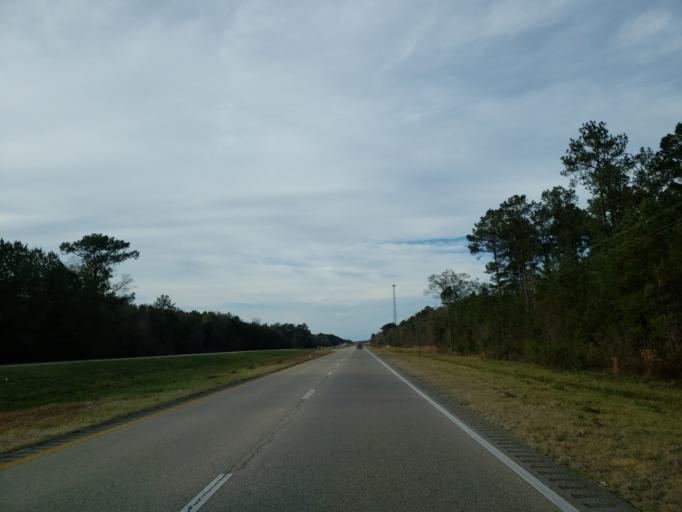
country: US
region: Mississippi
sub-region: Wayne County
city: Belmont
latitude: 31.6094
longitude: -88.5670
